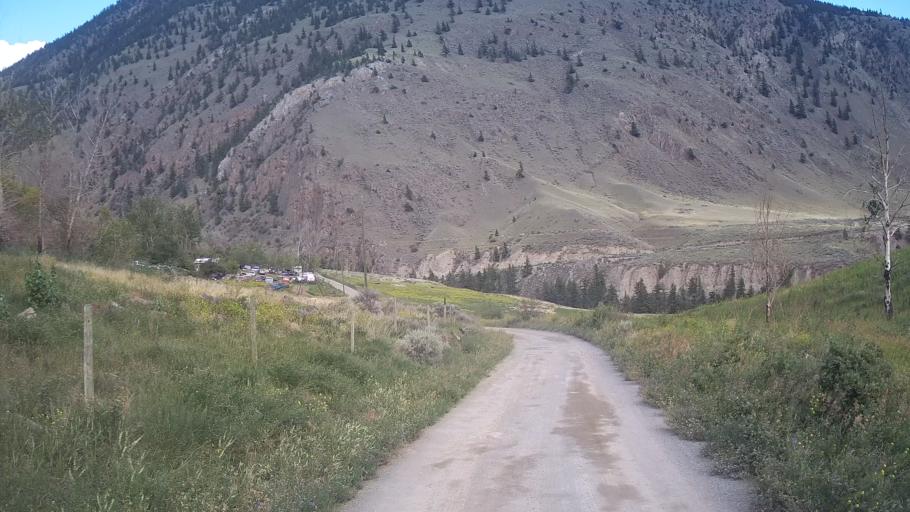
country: CA
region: British Columbia
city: Lillooet
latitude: 51.1974
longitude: -122.1092
